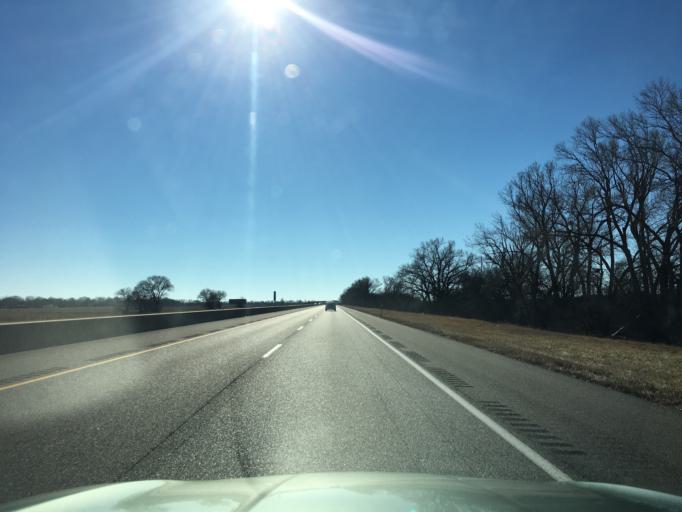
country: US
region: Kansas
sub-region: Sumner County
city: Belle Plaine
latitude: 37.4465
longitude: -97.3221
